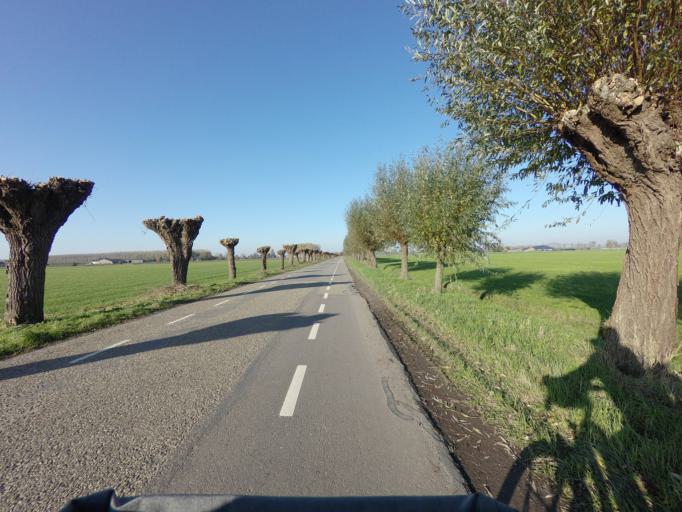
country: NL
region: North Brabant
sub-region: Gemeente Waalwijk
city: Waalwijk
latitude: 51.7538
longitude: 5.0553
